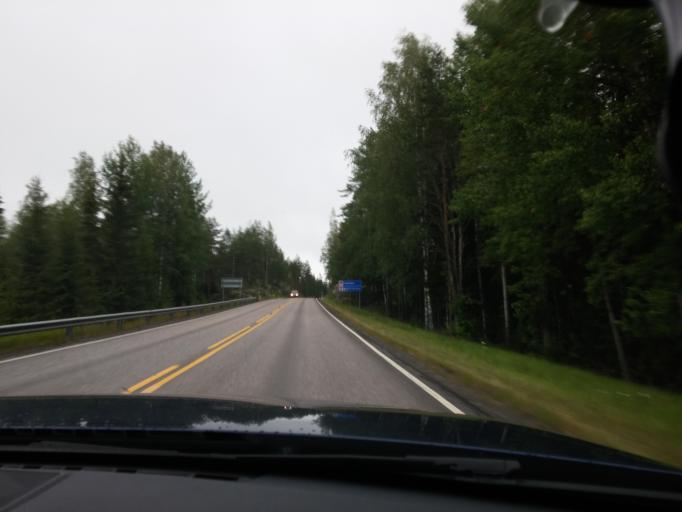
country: FI
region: Pirkanmaa
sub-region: Ylae-Pirkanmaa
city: Vilppula
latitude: 61.9304
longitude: 24.5408
